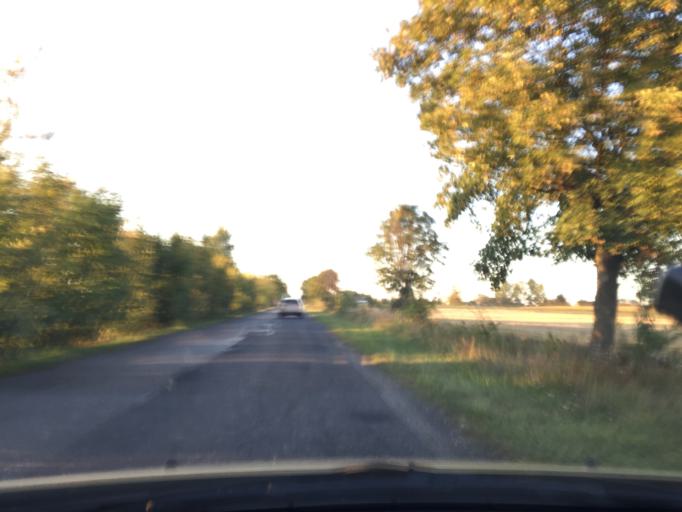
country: PL
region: Greater Poland Voivodeship
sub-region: Powiat pleszewski
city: Dobrzyca
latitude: 51.8372
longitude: 17.6205
